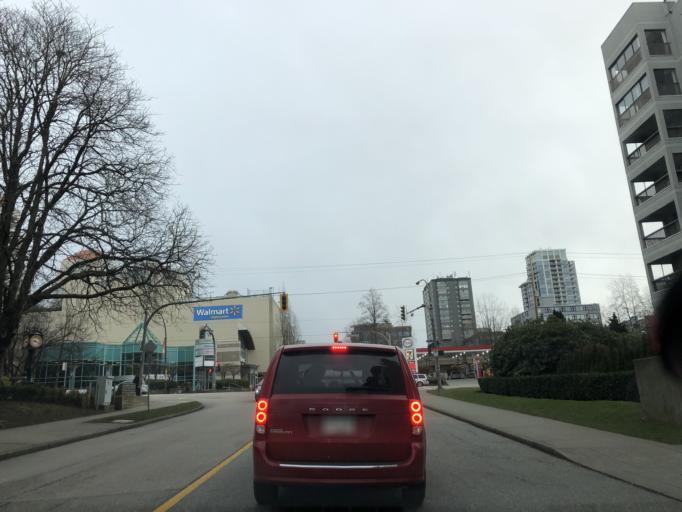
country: CA
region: British Columbia
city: New Westminster
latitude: 49.2108
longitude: -122.9246
